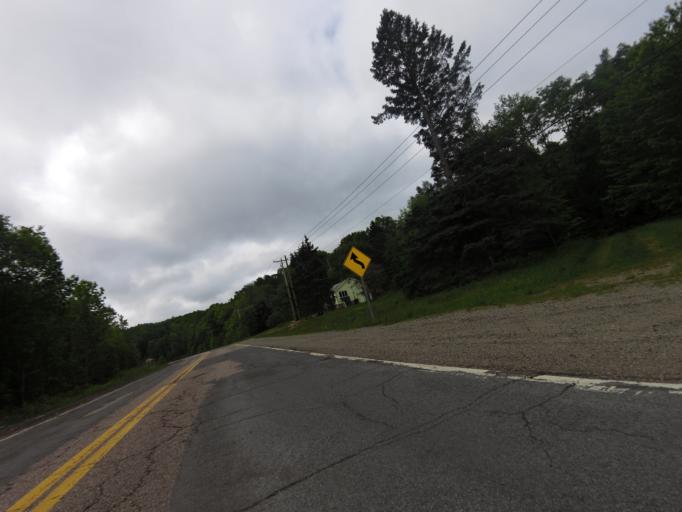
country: CA
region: Quebec
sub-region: Outaouais
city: Shawville
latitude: 45.8333
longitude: -76.4614
